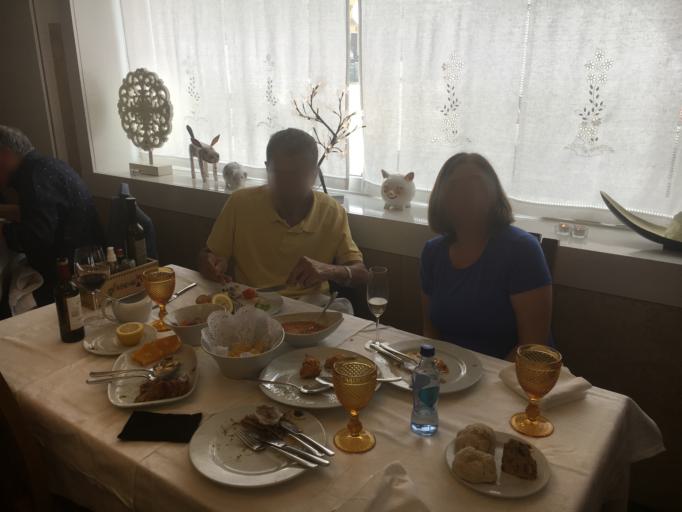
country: PT
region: Aveiro
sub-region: Mealhada
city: Mealhada
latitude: 40.3901
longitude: -8.4508
